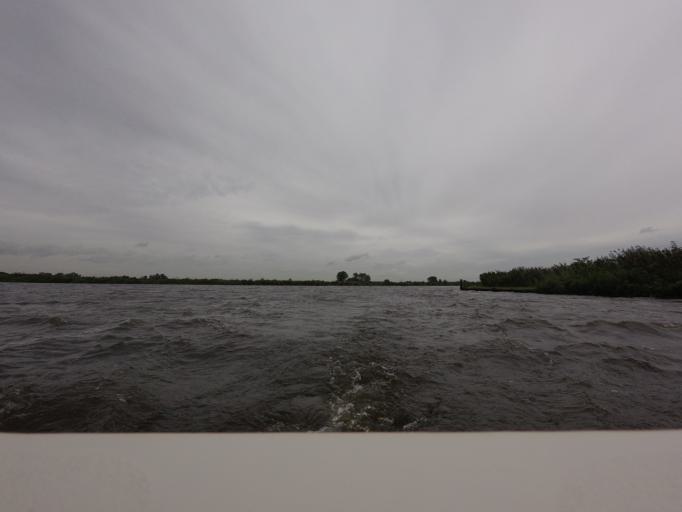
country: NL
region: Friesland
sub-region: Gemeente Boarnsterhim
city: Grou
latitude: 53.1090
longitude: 5.8596
